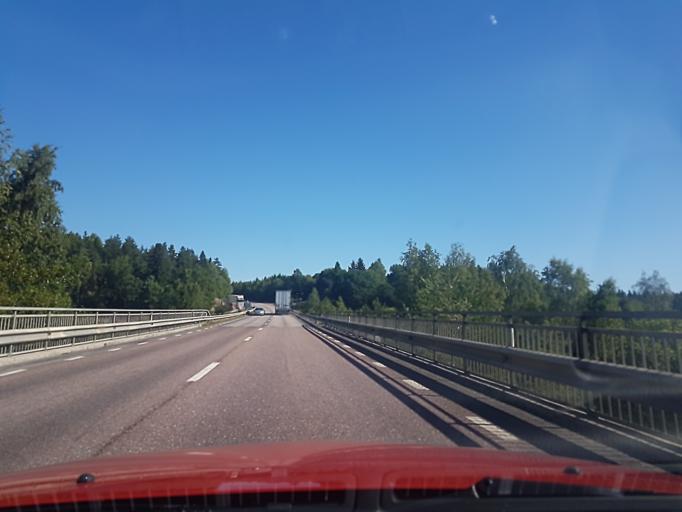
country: SE
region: Soedermanland
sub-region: Strangnas Kommun
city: Strangnas
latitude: 59.3998
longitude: 17.0151
